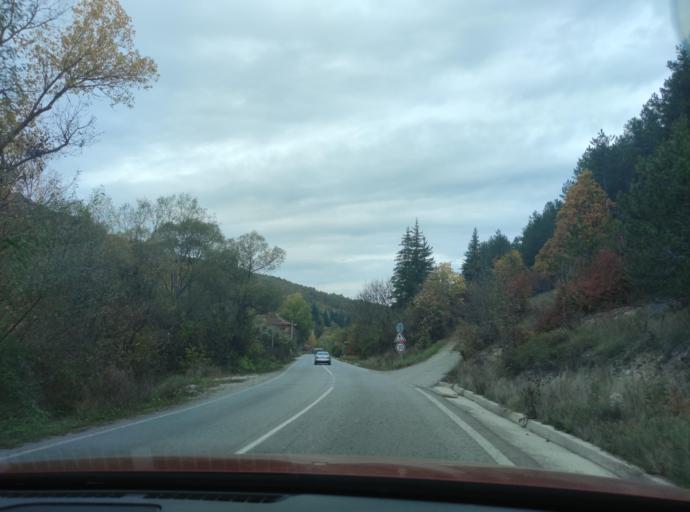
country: BG
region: Sofiya
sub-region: Obshtina Godech
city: Godech
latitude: 42.9692
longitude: 23.1455
